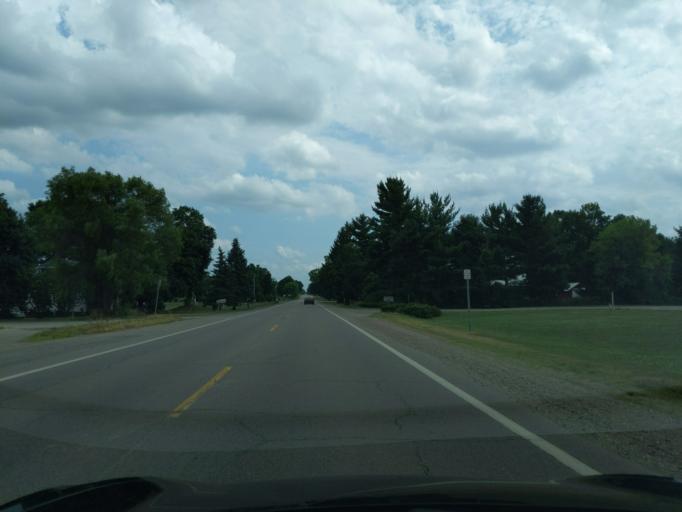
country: US
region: Michigan
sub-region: Eaton County
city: Eaton Rapids
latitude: 42.4793
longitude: -84.6598
